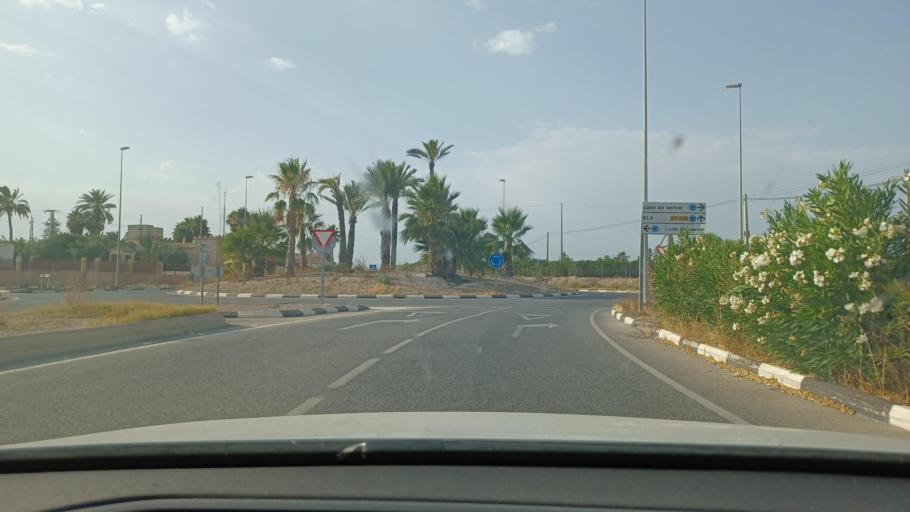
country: ES
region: Valencia
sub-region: Provincia de Alicante
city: Elche
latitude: 38.2212
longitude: -0.6976
